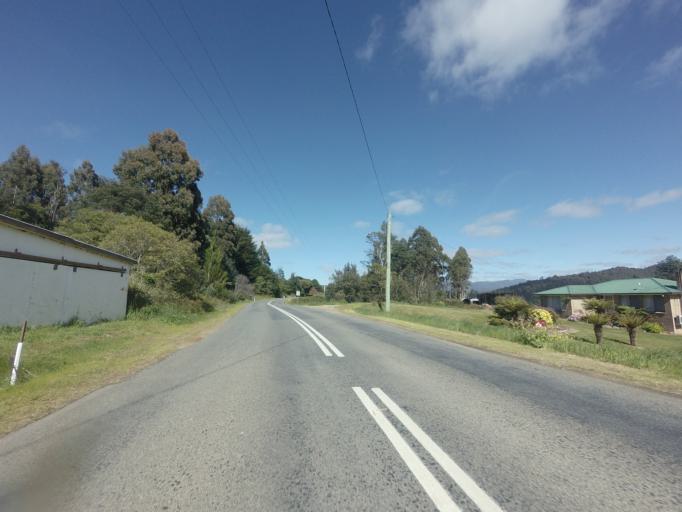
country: AU
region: Tasmania
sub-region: Derwent Valley
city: New Norfolk
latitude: -42.7504
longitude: 146.6423
